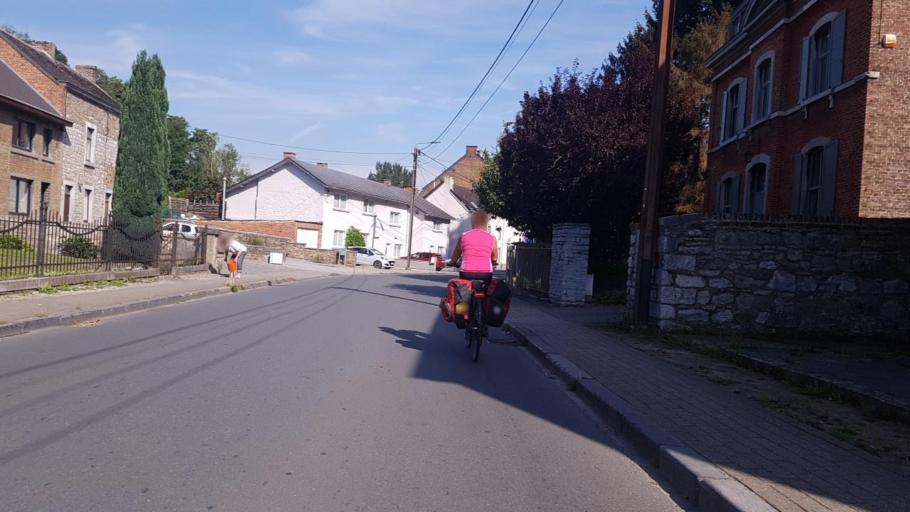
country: BE
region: Wallonia
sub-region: Province de Namur
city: Floreffe
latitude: 50.4405
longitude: 4.7951
